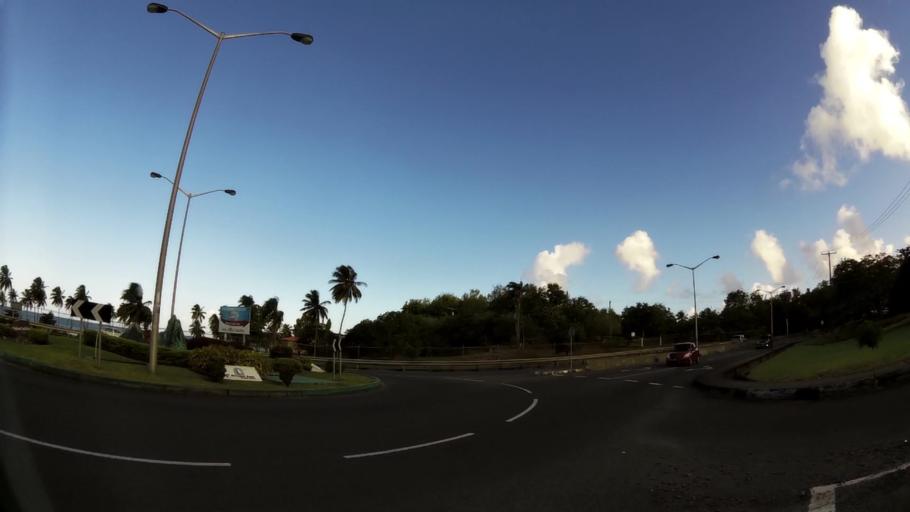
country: LC
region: Castries Quarter
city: Bisee
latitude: 14.0289
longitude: -60.9783
